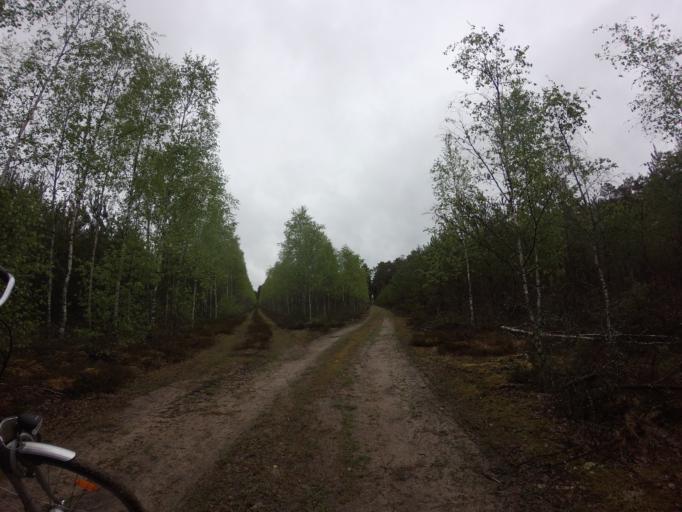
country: PL
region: West Pomeranian Voivodeship
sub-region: Powiat drawski
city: Kalisz Pomorski
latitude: 53.2153
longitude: 16.0087
